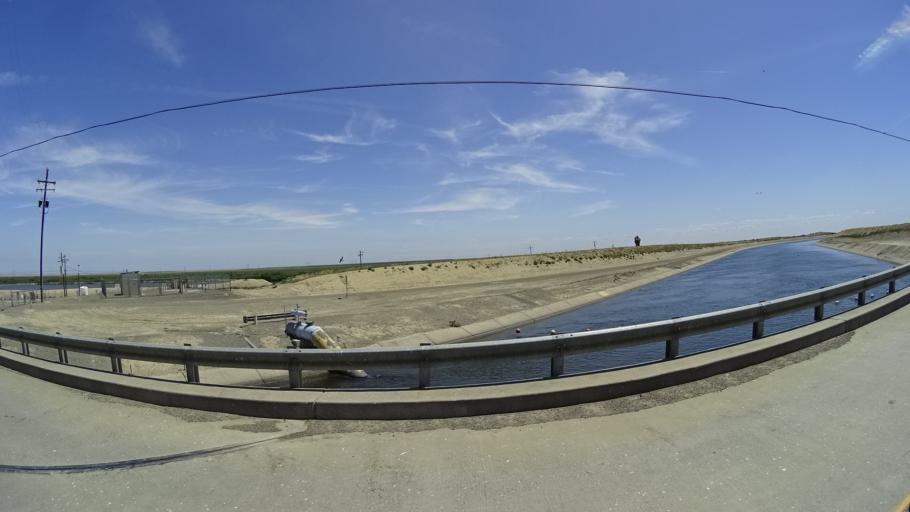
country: US
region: California
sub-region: Kings County
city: Kettleman City
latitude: 35.9063
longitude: -119.9150
